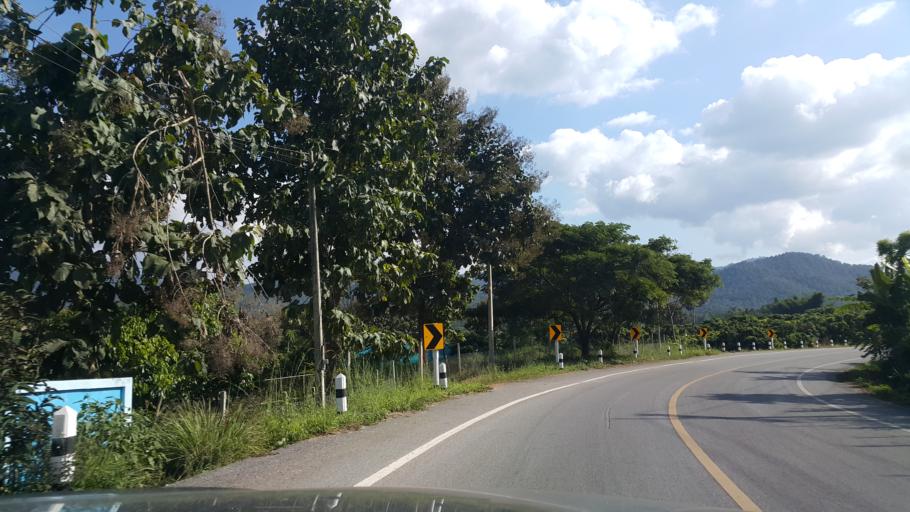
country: TH
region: Lamphun
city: Mae Tha
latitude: 18.5355
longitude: 99.2337
